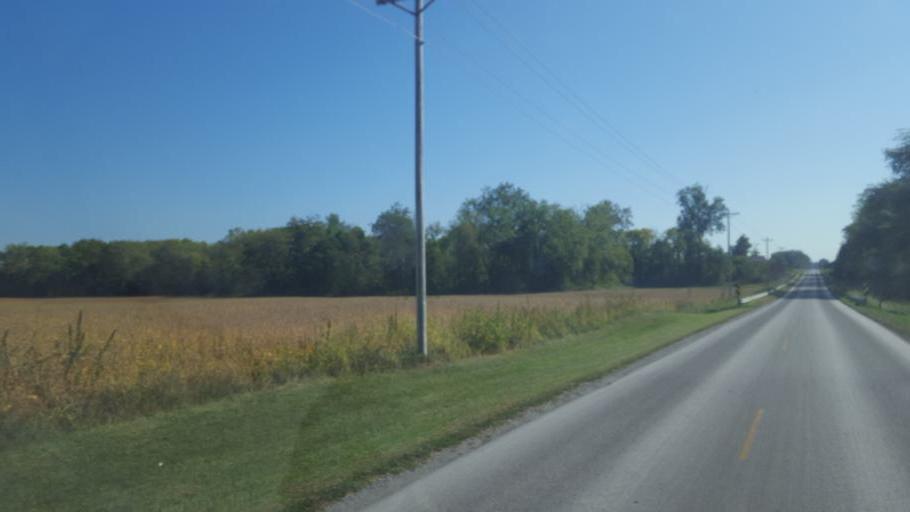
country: US
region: Ohio
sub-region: Hardin County
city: Kenton
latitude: 40.5846
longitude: -83.5004
